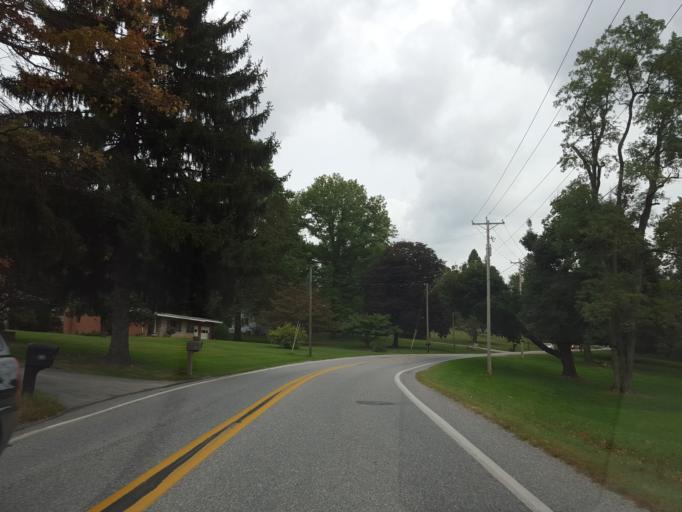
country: US
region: Pennsylvania
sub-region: York County
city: Red Lion
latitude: 39.8906
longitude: -76.6010
